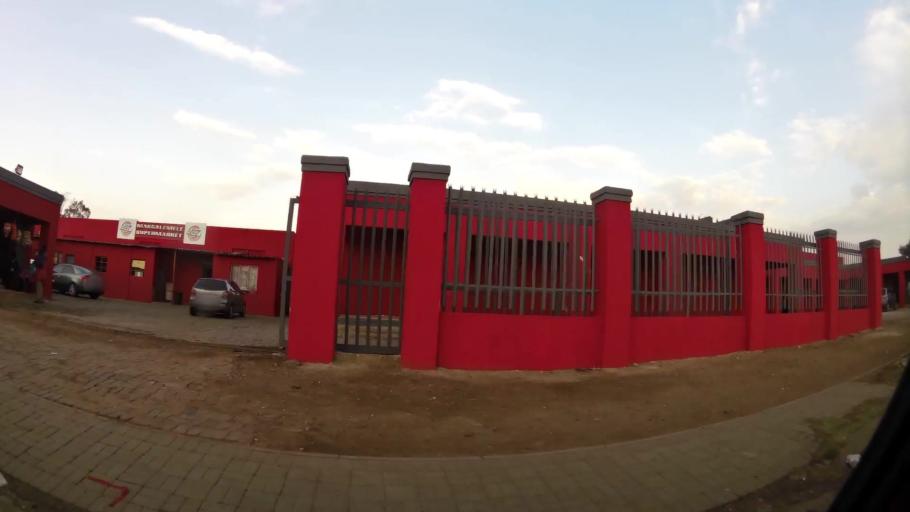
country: ZA
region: Gauteng
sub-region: City of Johannesburg Metropolitan Municipality
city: Orange Farm
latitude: -26.5507
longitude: 27.8408
